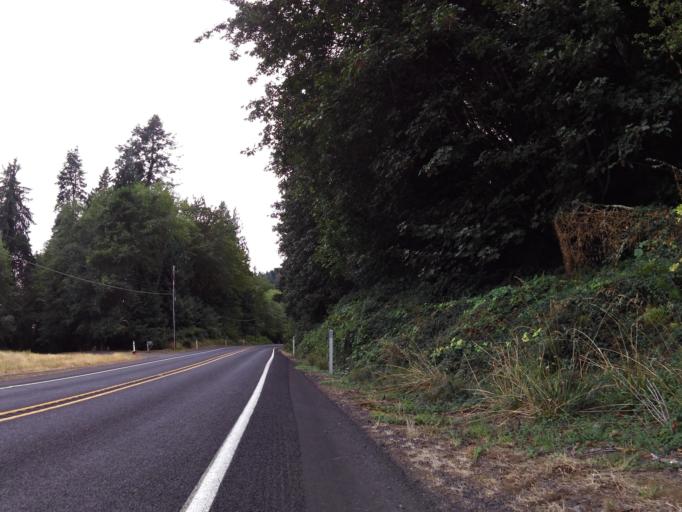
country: US
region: Oregon
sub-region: Columbia County
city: Clatskanie
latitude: 46.1737
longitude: -123.2277
